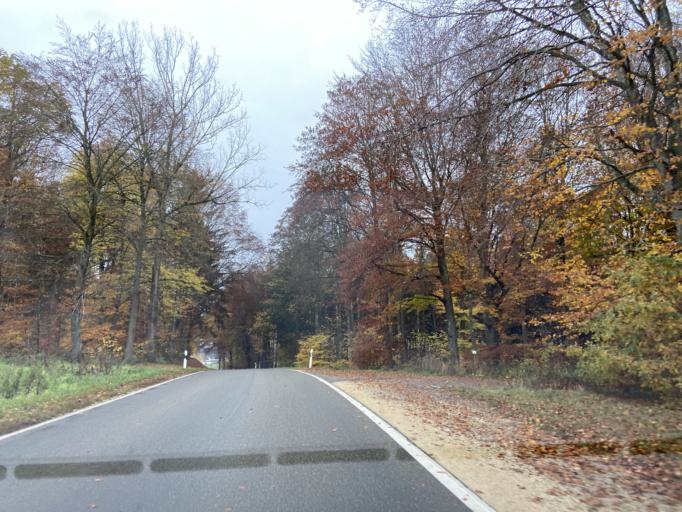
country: DE
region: Baden-Wuerttemberg
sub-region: Tuebingen Region
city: Wald
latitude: 47.9651
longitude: 9.1900
